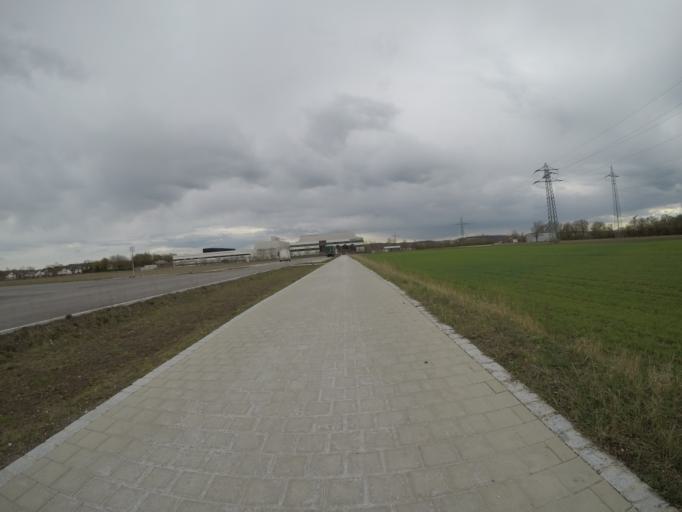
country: DE
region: Bavaria
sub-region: Lower Bavaria
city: Tiefenbach
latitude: 48.5457
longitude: 12.1104
